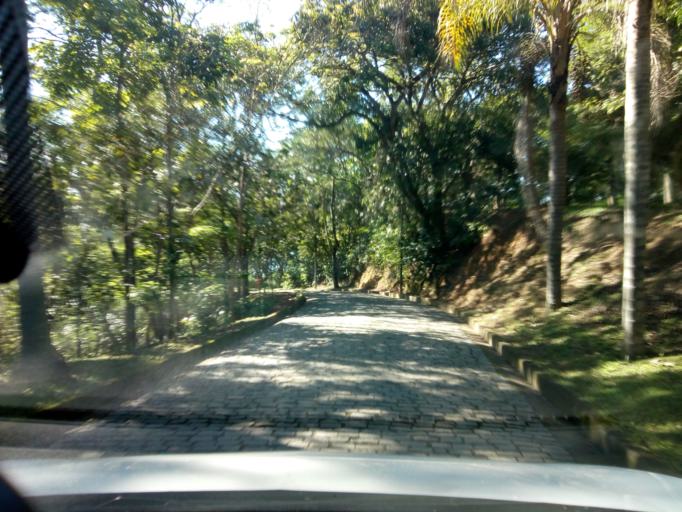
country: BR
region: Rio de Janeiro
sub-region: Rio De Janeiro
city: Rio de Janeiro
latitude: -22.9889
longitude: -43.2310
